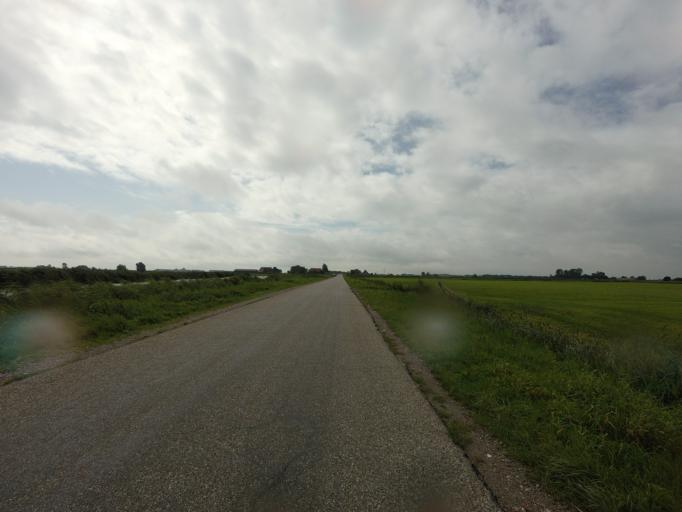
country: NL
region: Friesland
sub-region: Sudwest Fryslan
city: Workum
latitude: 53.0042
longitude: 5.4725
